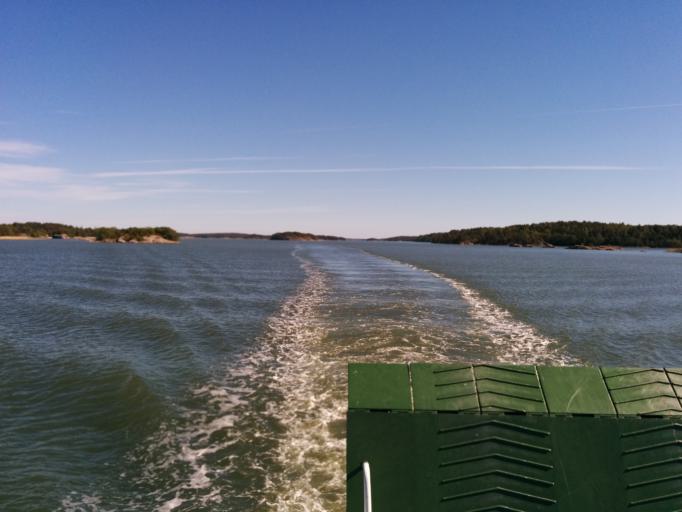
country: FI
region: Varsinais-Suomi
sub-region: Turku
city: Velkua
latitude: 60.4563
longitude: 21.7013
